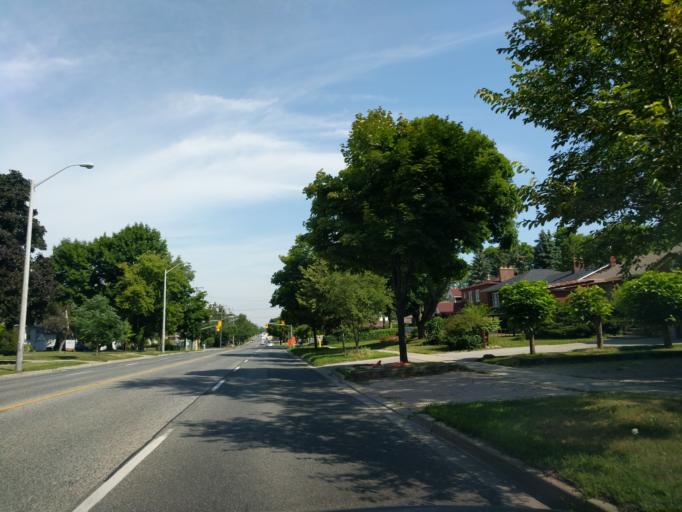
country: CA
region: Ontario
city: Scarborough
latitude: 43.7923
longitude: -79.2814
